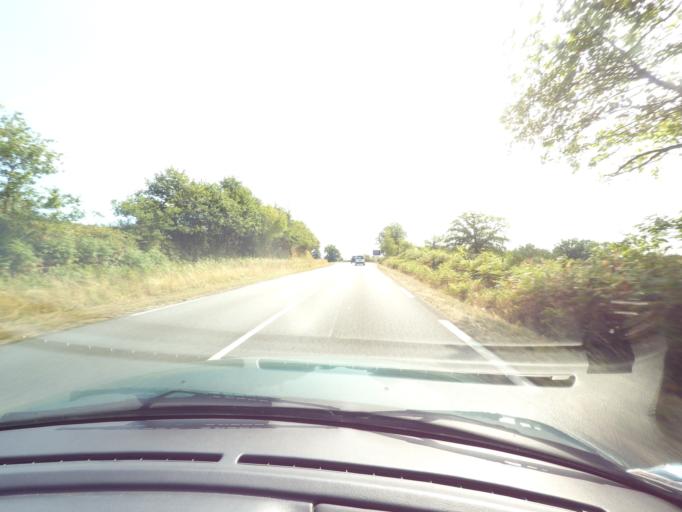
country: FR
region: Limousin
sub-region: Departement de la Haute-Vienne
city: Feytiat
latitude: 45.8055
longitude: 1.3628
